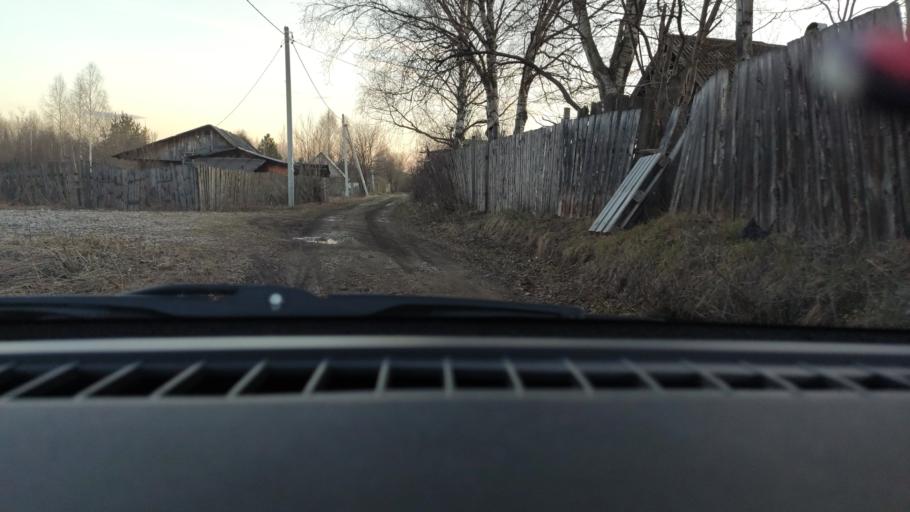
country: RU
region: Perm
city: Perm
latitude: 58.0813
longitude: 56.3184
